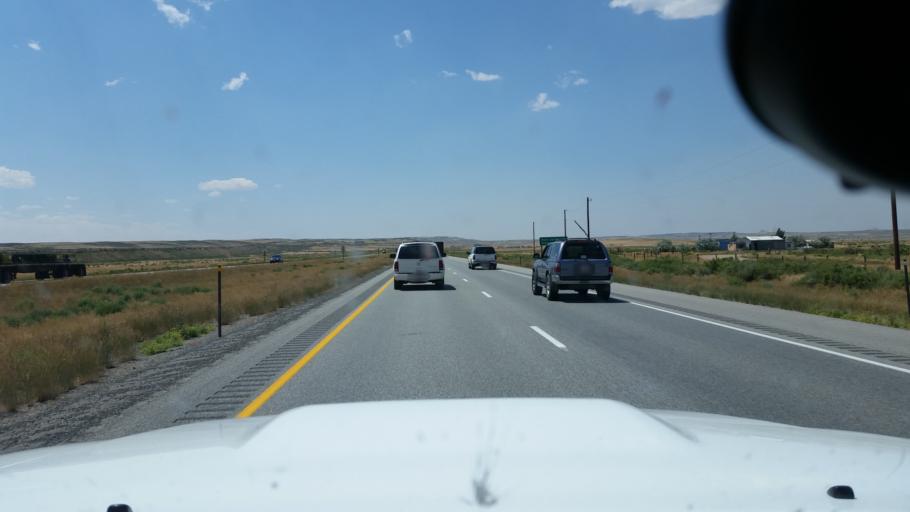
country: US
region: Wyoming
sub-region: Carbon County
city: Rawlins
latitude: 41.6494
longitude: -108.1396
